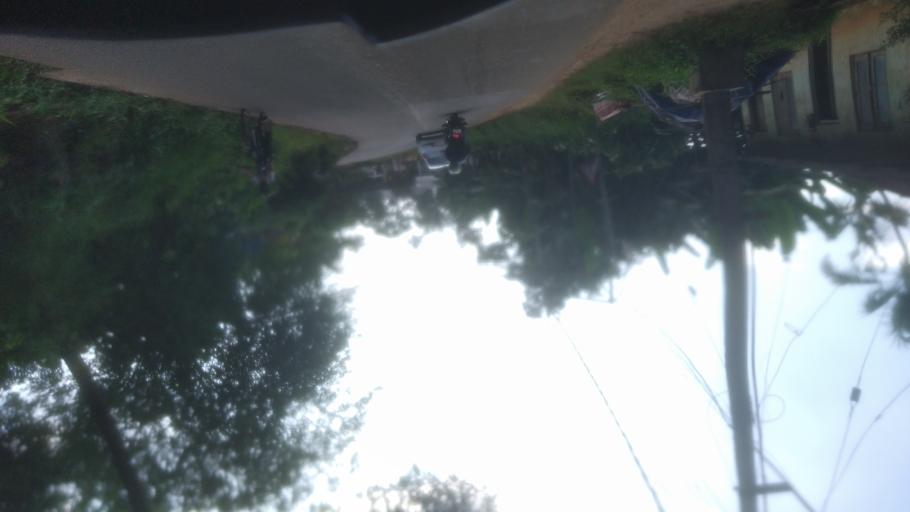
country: IN
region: Kerala
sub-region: Ernakulam
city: Muvattupula
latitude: 9.9954
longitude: 76.6059
